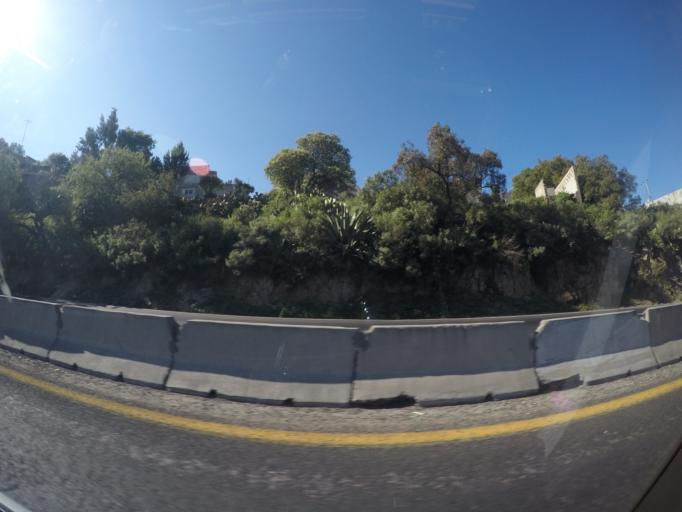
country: MX
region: Hidalgo
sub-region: Mineral de la Reforma
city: Colonia Militar
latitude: 20.1212
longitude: -98.6953
